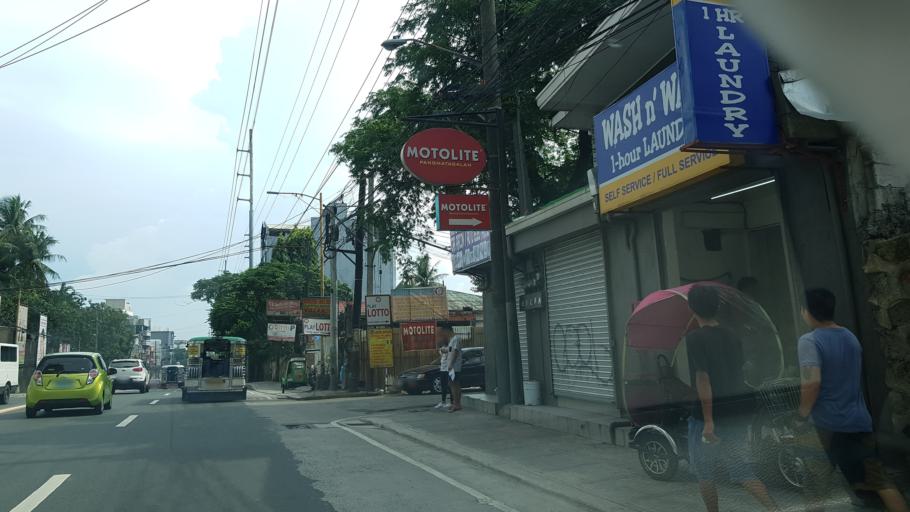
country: PH
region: Metro Manila
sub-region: Pasig
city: Pasig City
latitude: 14.5697
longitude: 121.0664
